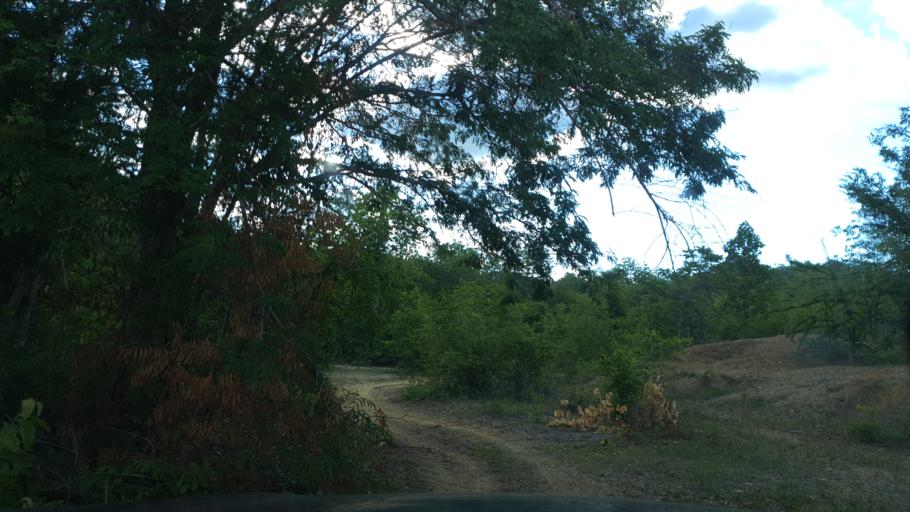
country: TH
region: Lampang
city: Sop Prap
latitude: 17.8862
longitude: 99.2900
